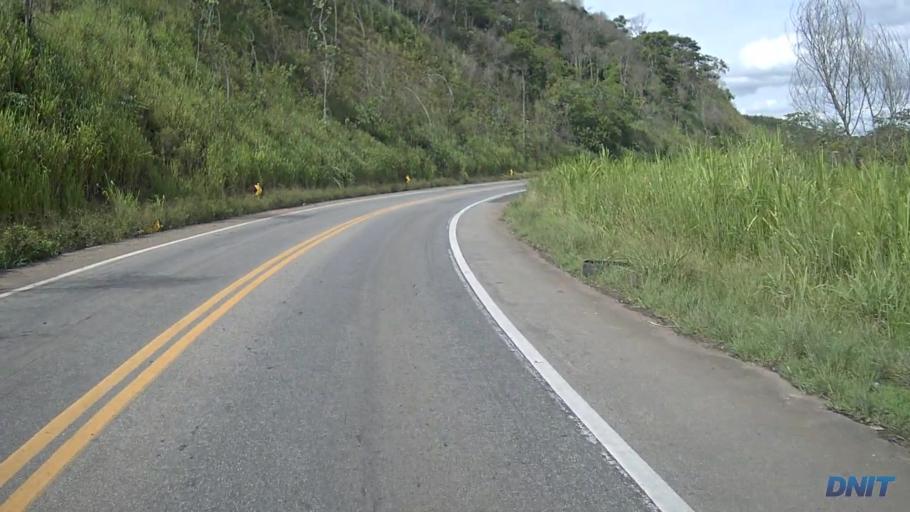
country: BR
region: Minas Gerais
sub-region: Ipaba
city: Ipaba
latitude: -19.3851
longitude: -42.4748
